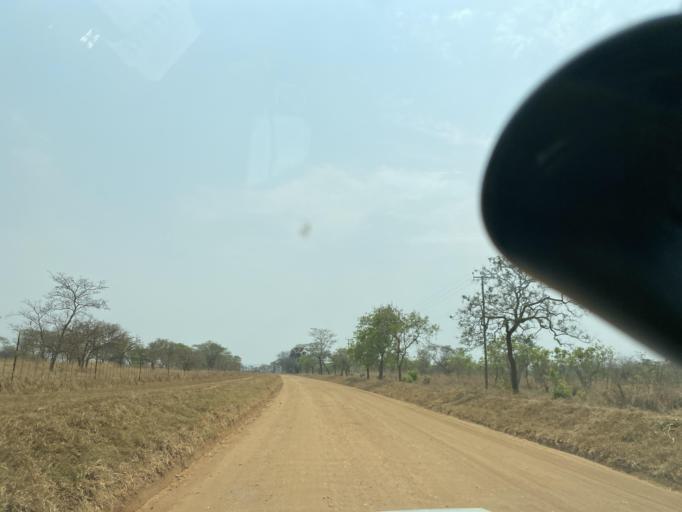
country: ZM
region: Lusaka
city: Kafue
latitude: -15.5973
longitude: 28.1125
